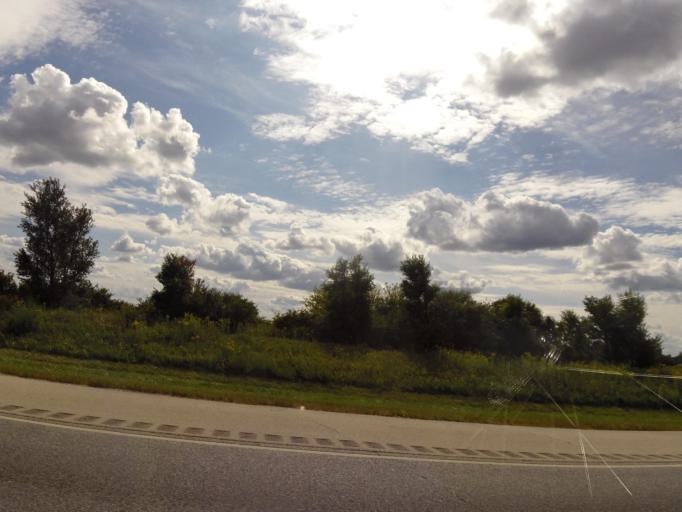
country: US
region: Illinois
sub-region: Kane County
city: Sugar Grove
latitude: 41.8139
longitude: -88.4515
